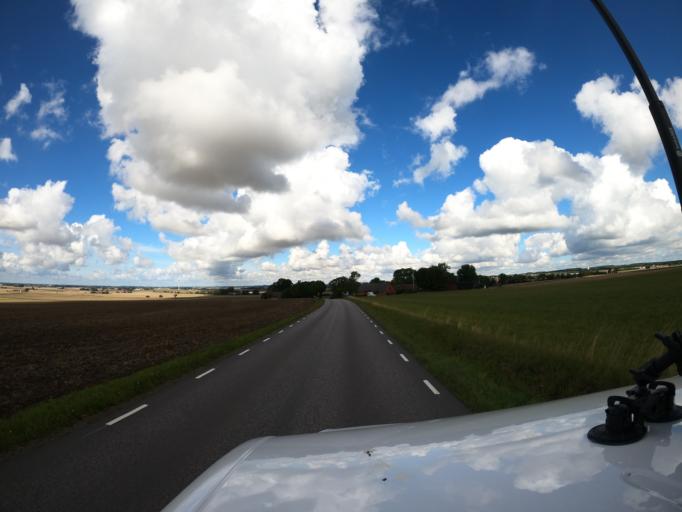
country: SE
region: Skane
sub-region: Lunds Kommun
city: Genarp
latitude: 55.6434
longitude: 13.3510
